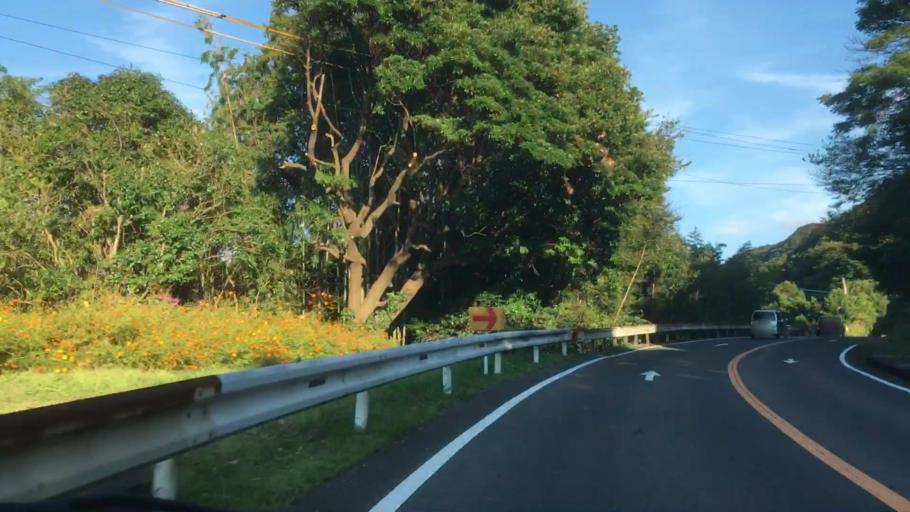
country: JP
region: Nagasaki
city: Sasebo
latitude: 33.0390
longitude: 129.6728
